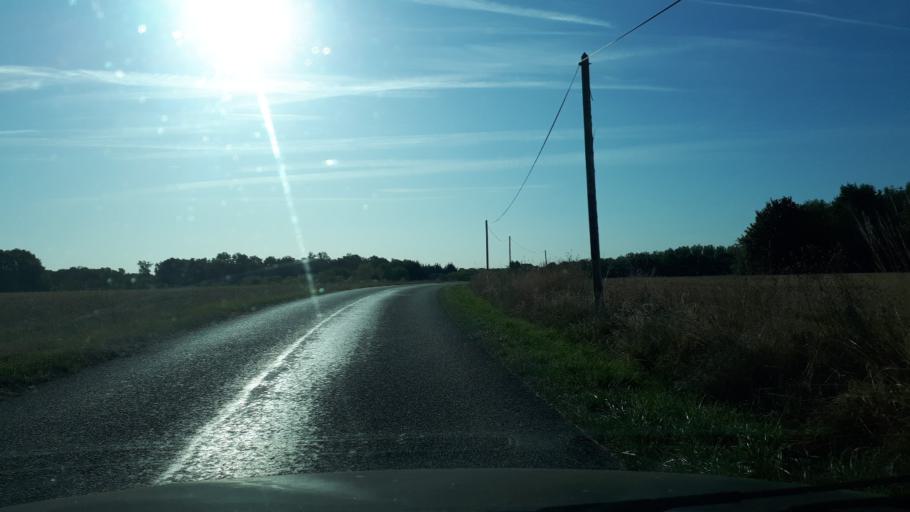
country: FR
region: Centre
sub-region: Departement d'Indre-et-Loire
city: Chateau-Renault
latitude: 47.6602
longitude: 0.9386
